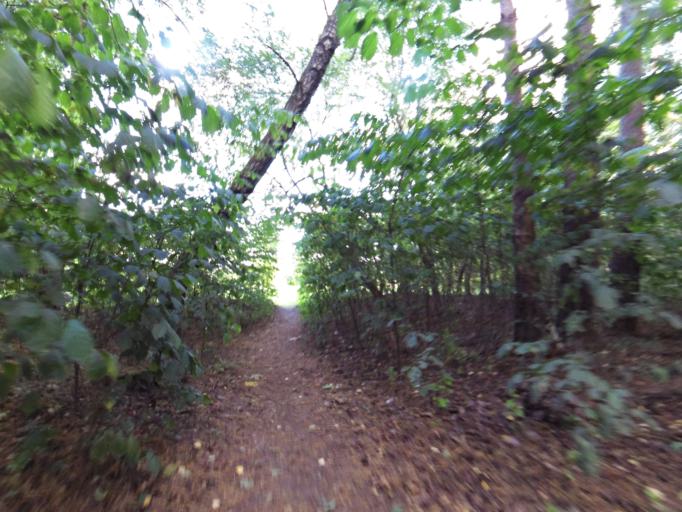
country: LT
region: Vilnius County
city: Justiniskes
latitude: 54.6931
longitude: 25.2277
